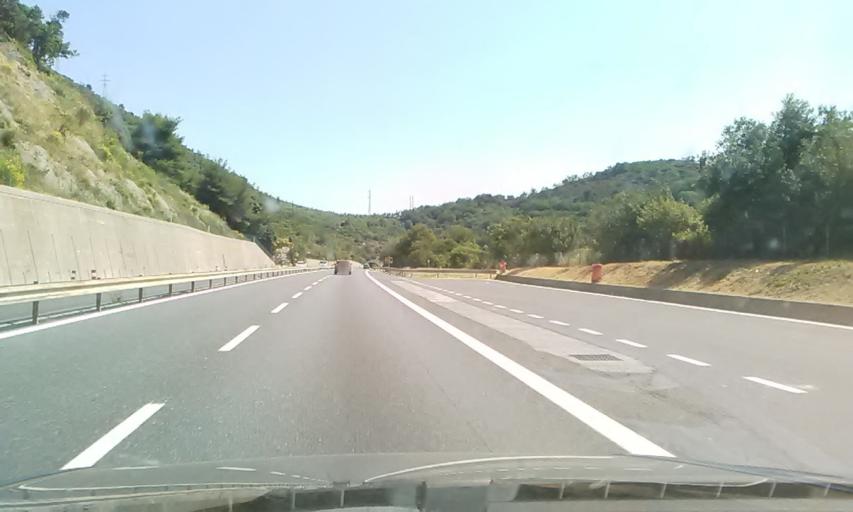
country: IT
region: Liguria
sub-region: Provincia di Savona
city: Loano
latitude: 44.1456
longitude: 8.2501
